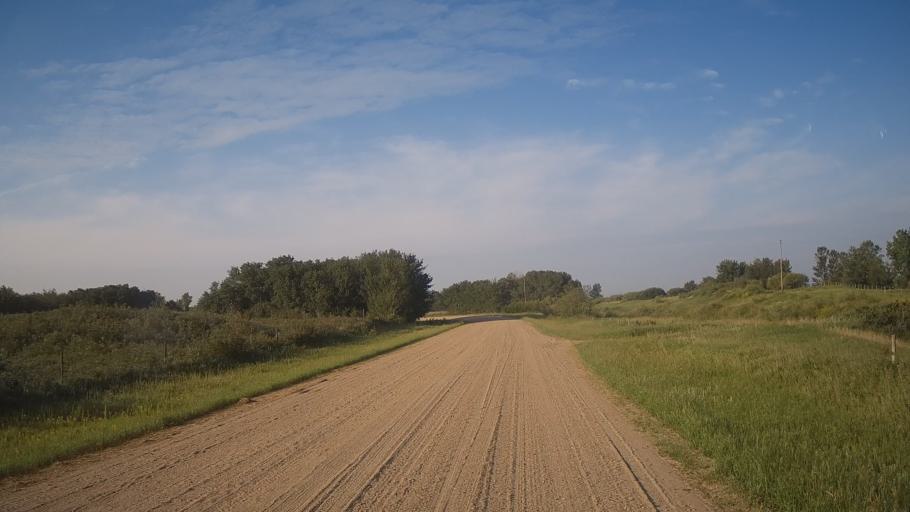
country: CA
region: Saskatchewan
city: Saskatoon
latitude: 51.8263
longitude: -106.5421
